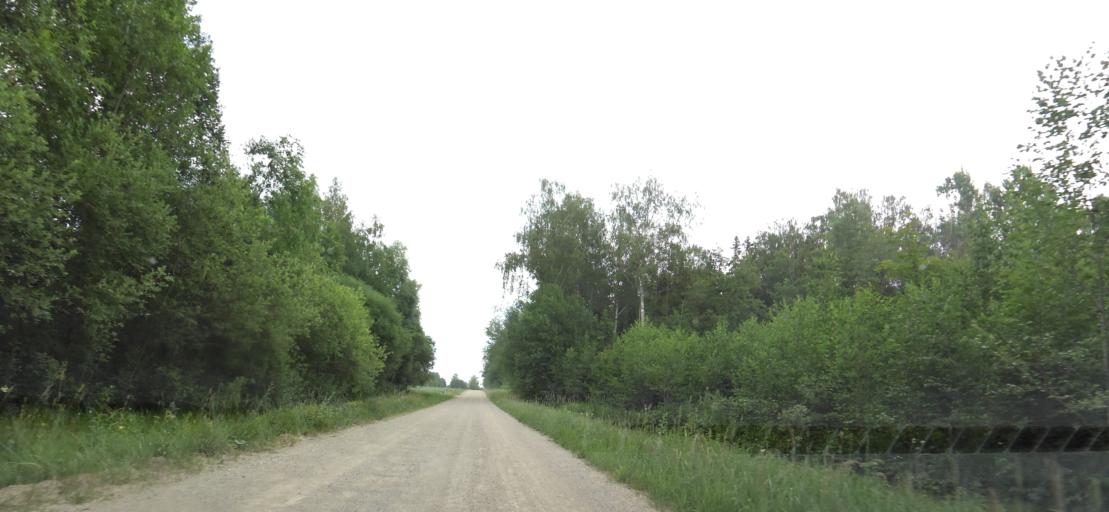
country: LT
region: Panevezys
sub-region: Birzai
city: Birzai
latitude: 56.2975
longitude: 24.9688
